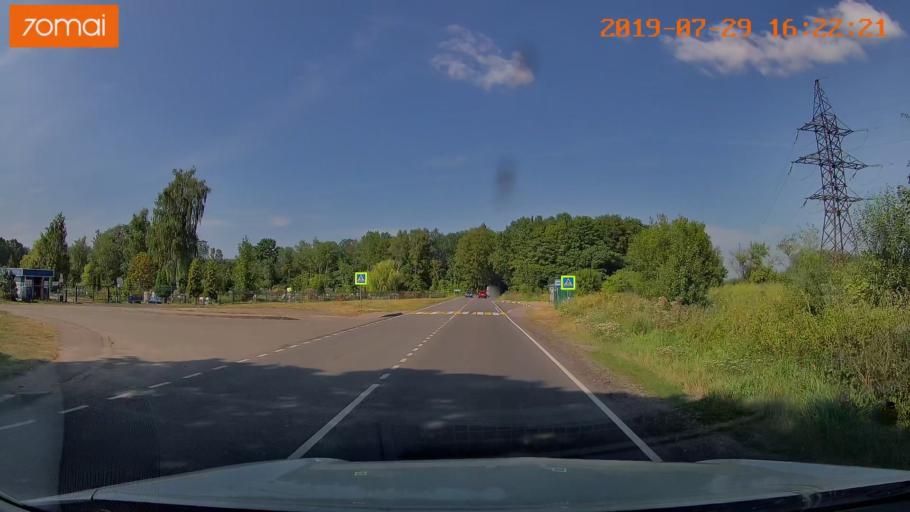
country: RU
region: Kaliningrad
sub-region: Gorod Kaliningrad
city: Baltiysk
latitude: 54.6972
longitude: 19.9385
